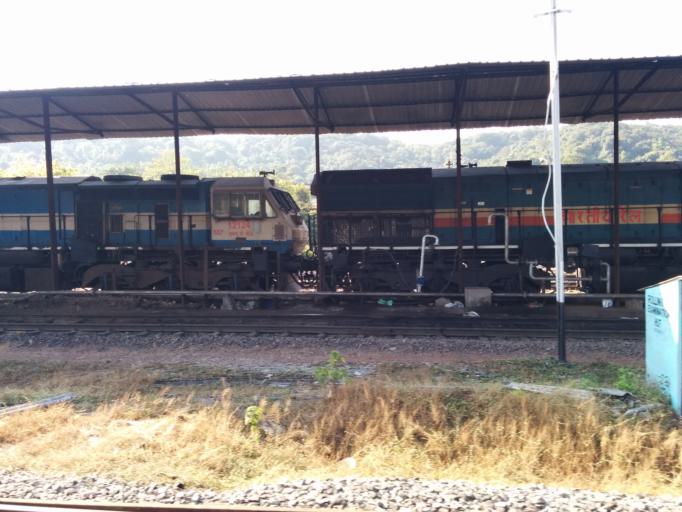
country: IN
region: Karnataka
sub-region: Belgaum
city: Londa
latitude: 15.3990
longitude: 74.3304
